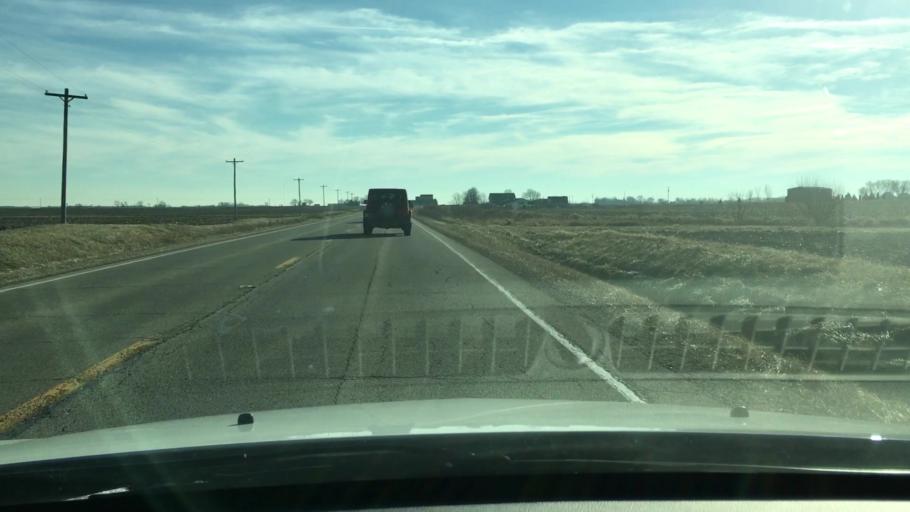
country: US
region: Illinois
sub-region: LaSalle County
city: Mendota
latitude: 41.4907
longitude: -89.1272
